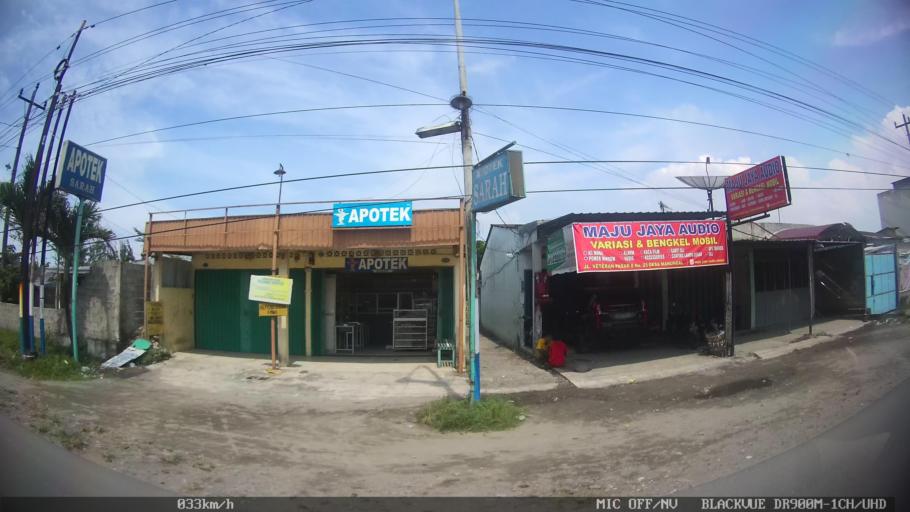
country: ID
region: North Sumatra
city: Labuhan Deli
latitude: 3.6621
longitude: 98.6564
